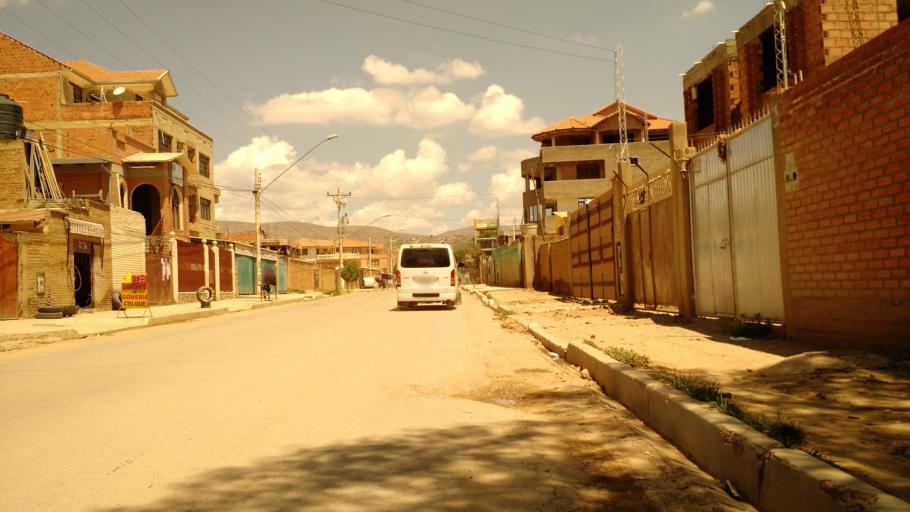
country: BO
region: Cochabamba
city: Cochabamba
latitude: -17.4446
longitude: -66.1554
